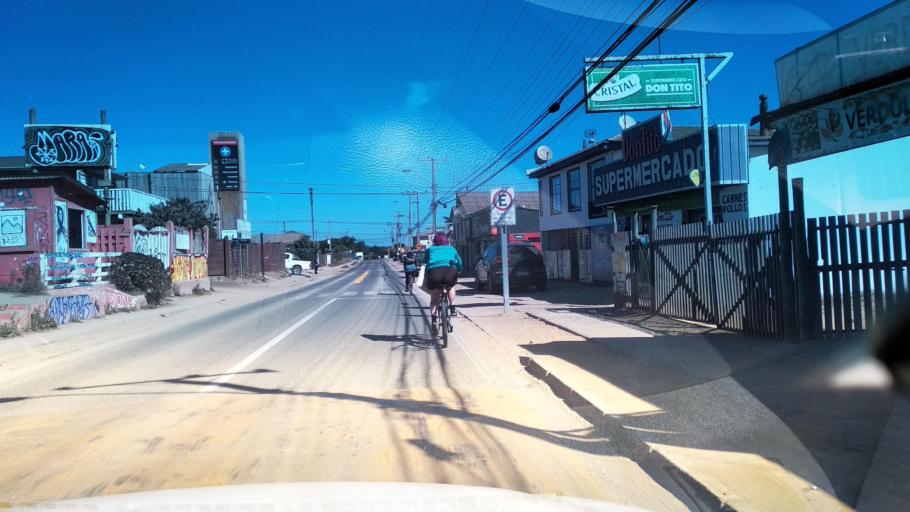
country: CL
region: O'Higgins
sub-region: Provincia de Colchagua
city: Santa Cruz
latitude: -34.4033
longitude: -72.0247
